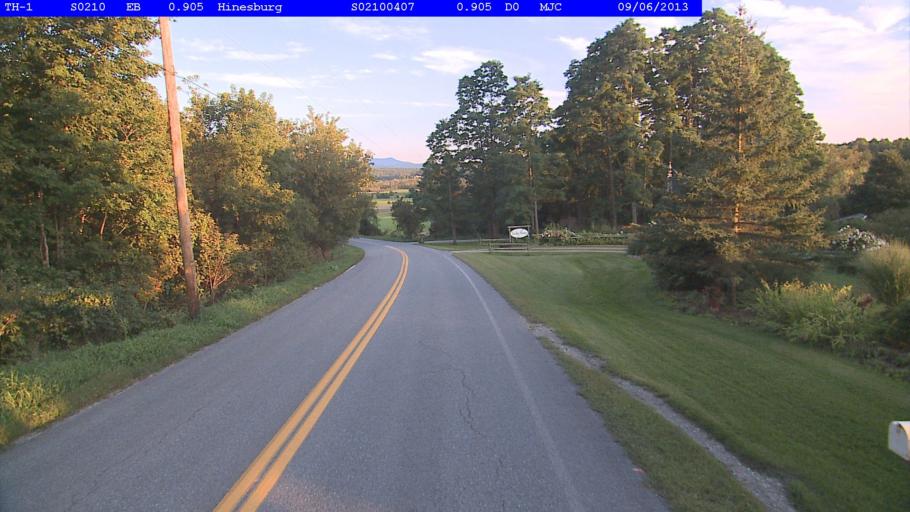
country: US
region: Vermont
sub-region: Chittenden County
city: Hinesburg
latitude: 44.3516
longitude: -73.1522
